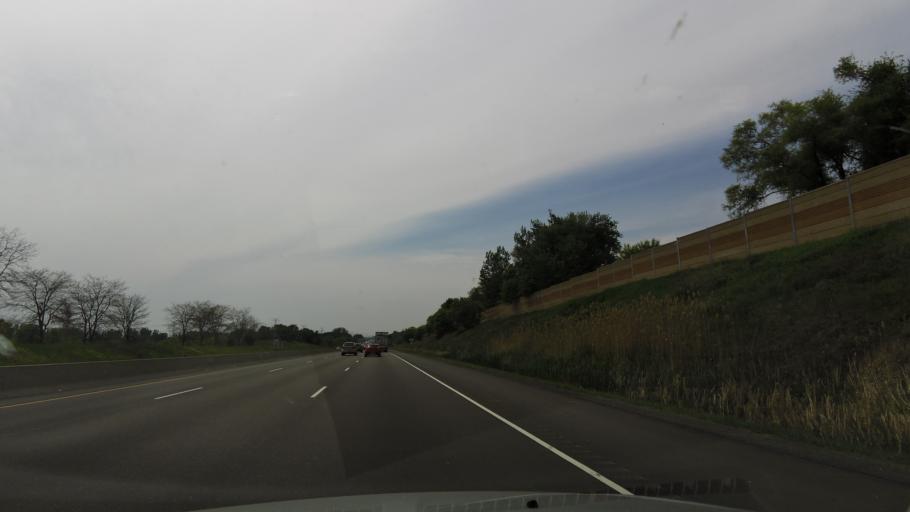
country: CA
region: Ontario
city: Oshawa
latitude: 43.9088
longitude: -78.5952
